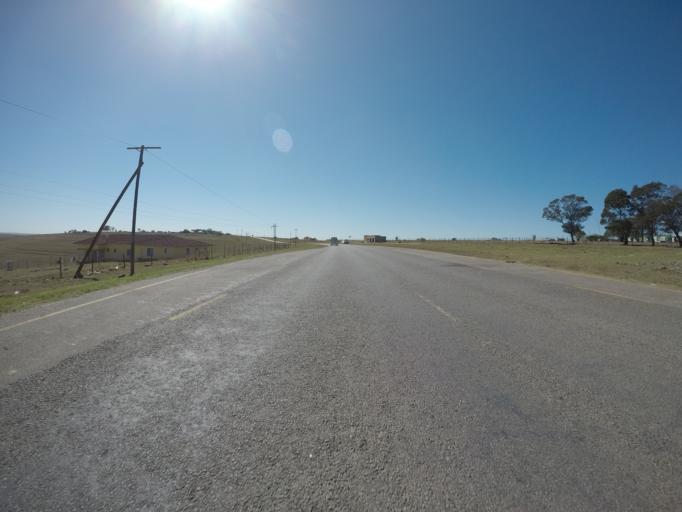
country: ZA
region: Eastern Cape
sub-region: OR Tambo District Municipality
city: Mthatha
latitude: -31.8924
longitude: 28.7693
